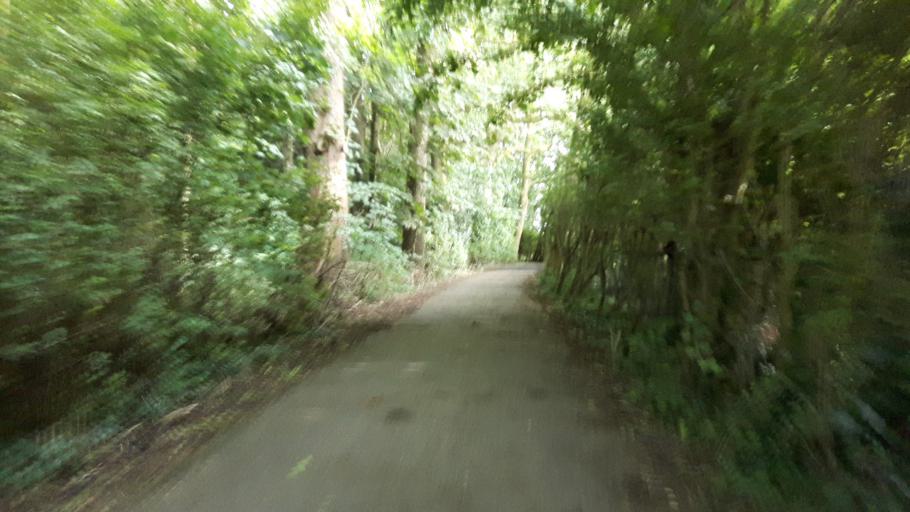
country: NL
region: Utrecht
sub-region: Gemeente Montfoort
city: Montfoort
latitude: 52.0960
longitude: 4.9688
